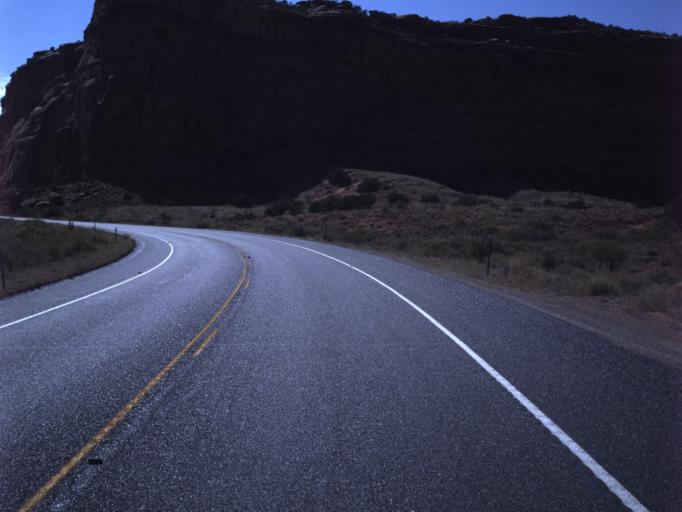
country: US
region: Utah
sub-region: Grand County
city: Moab
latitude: 38.6574
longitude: -109.7129
